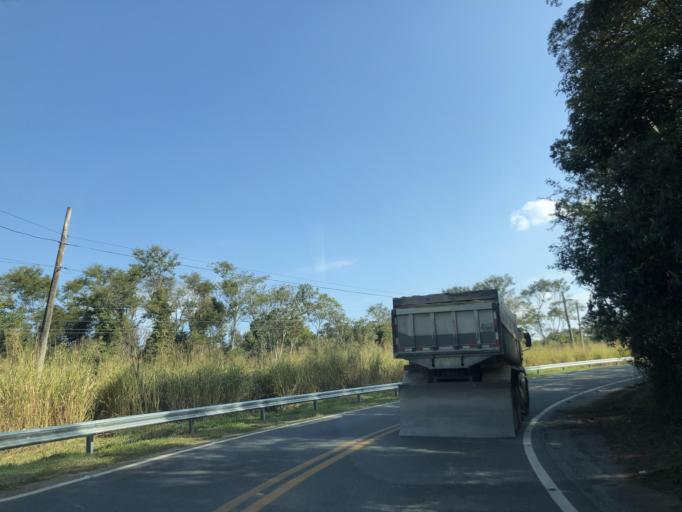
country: BR
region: Sao Paulo
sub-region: Pilar Do Sul
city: Pilar do Sul
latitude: -23.8089
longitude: -47.6949
